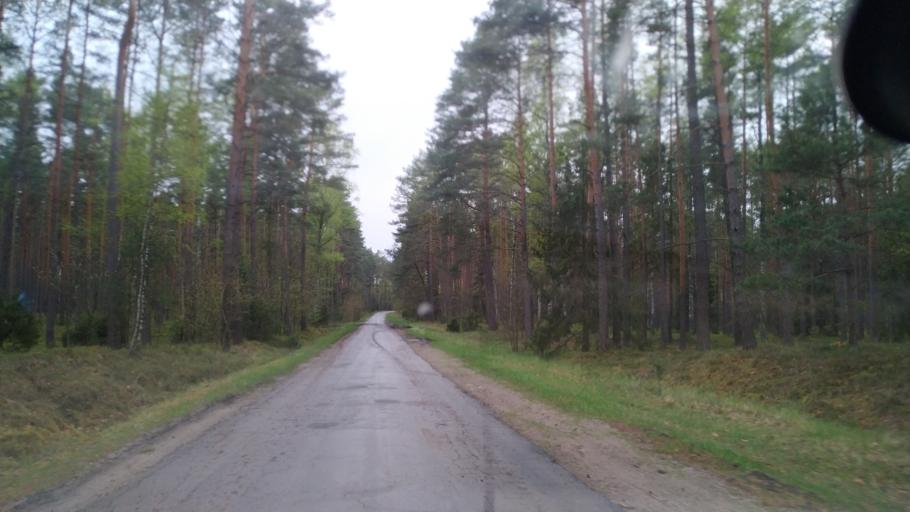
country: PL
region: Pomeranian Voivodeship
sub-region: Powiat starogardzki
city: Osiek
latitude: 53.6828
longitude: 18.5045
